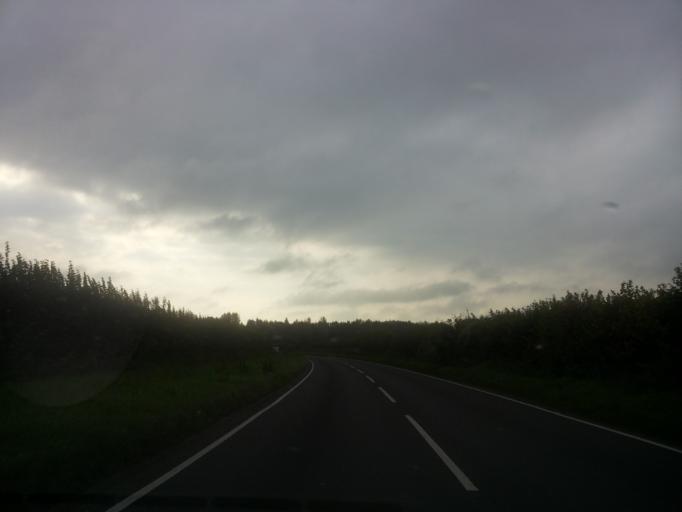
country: GB
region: England
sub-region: Buckinghamshire
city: Wendover
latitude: 51.7397
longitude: -0.7338
